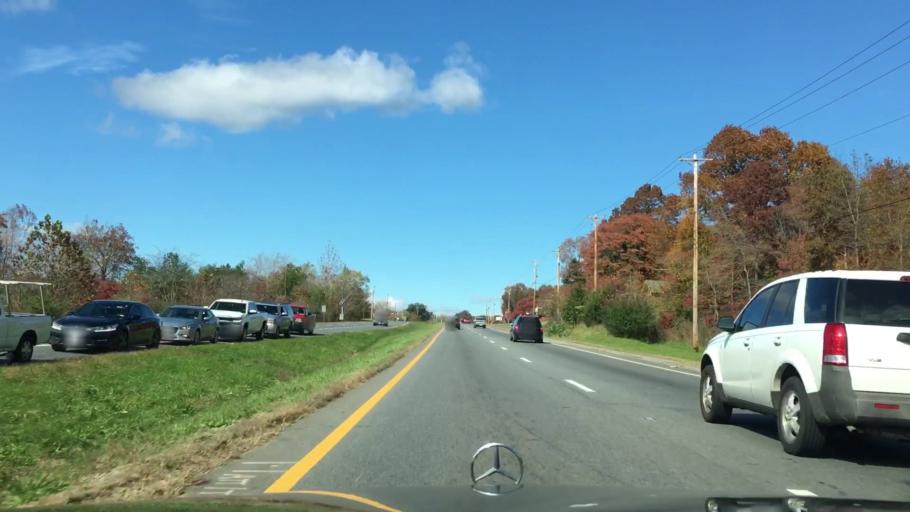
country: US
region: Virginia
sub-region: Campbell County
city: Timberlake
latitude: 37.3125
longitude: -79.1845
